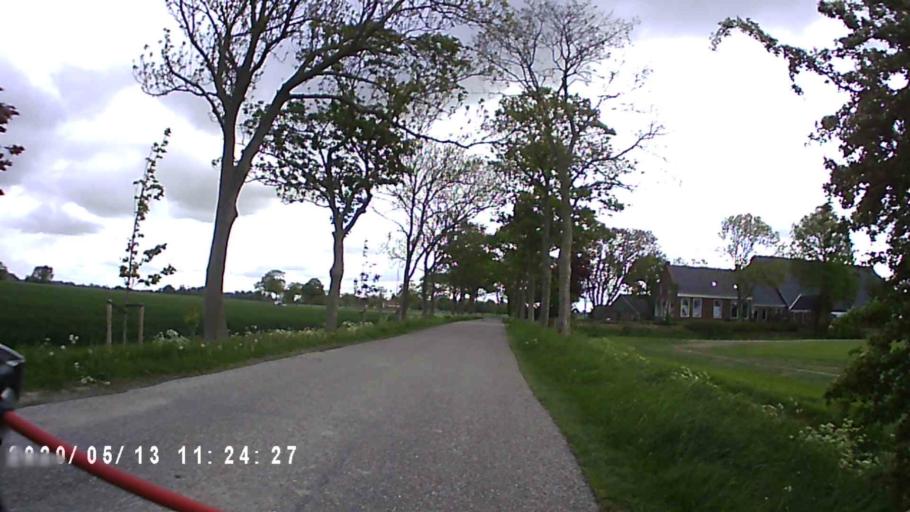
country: NL
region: Groningen
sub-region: Gemeente Zuidhorn
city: Oldehove
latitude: 53.3118
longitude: 6.4077
